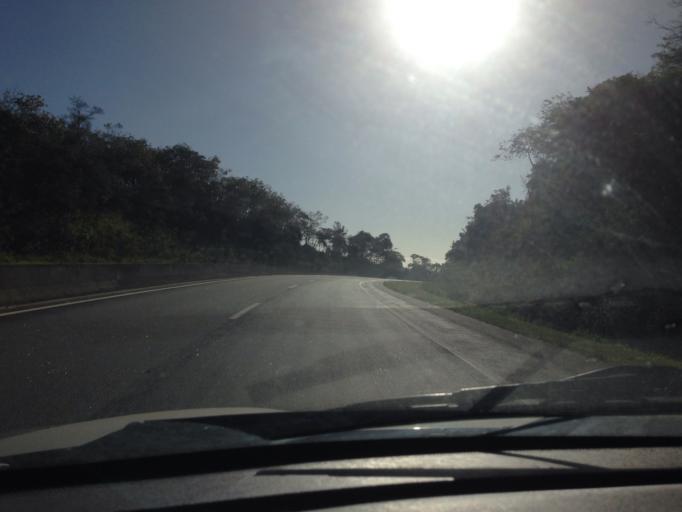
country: BR
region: Espirito Santo
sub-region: Guarapari
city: Guarapari
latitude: -20.6280
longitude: -40.5068
